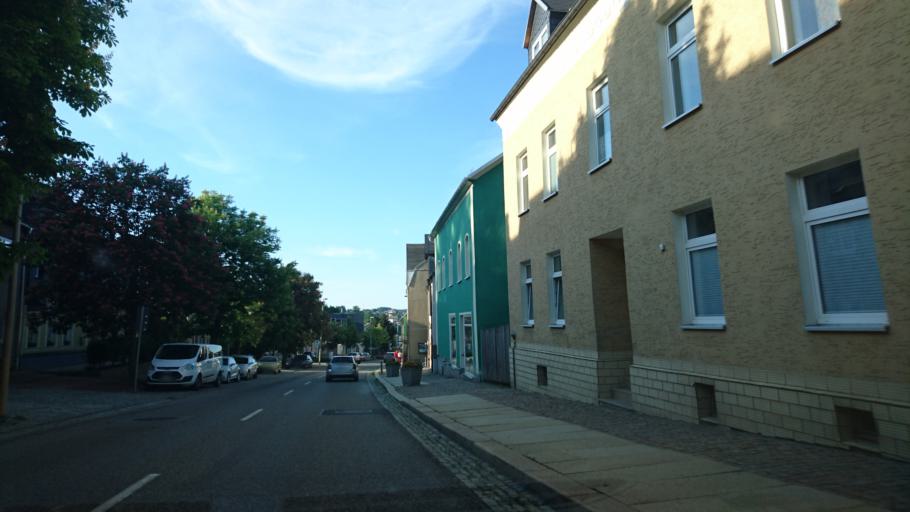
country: DE
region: Saxony
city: Schneeberg
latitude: 50.5834
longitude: 12.6350
